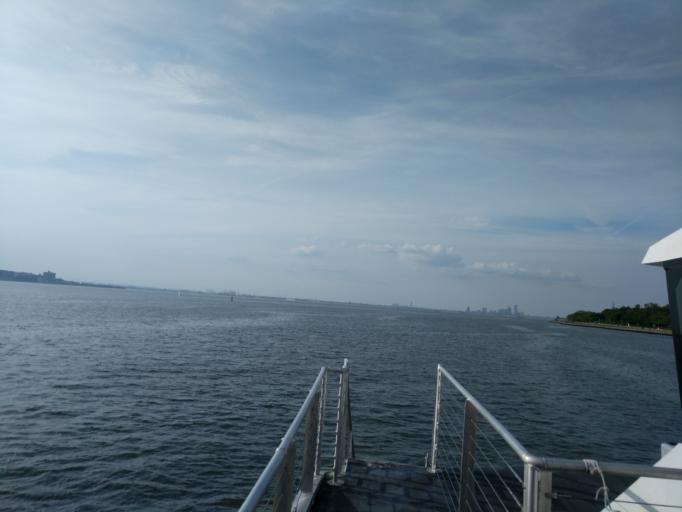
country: US
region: New York
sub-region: Kings County
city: Bensonhurst
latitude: 40.6172
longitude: -74.0429
